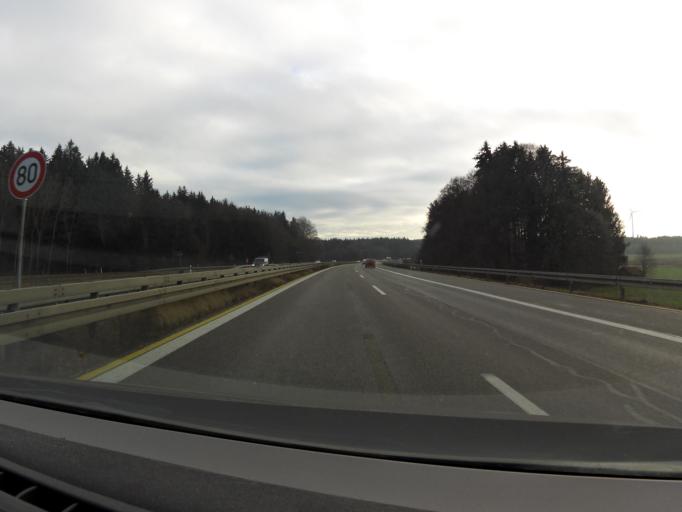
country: DE
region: Bavaria
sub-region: Upper Bavaria
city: Schaftlarn
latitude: 47.9941
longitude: 11.4289
